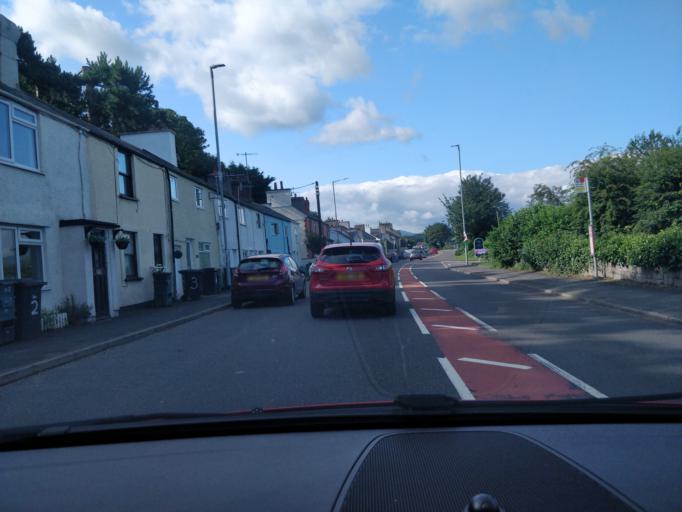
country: GB
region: Wales
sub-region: Conwy
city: Llansantffraid Glan Conwy
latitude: 53.2704
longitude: -3.7950
